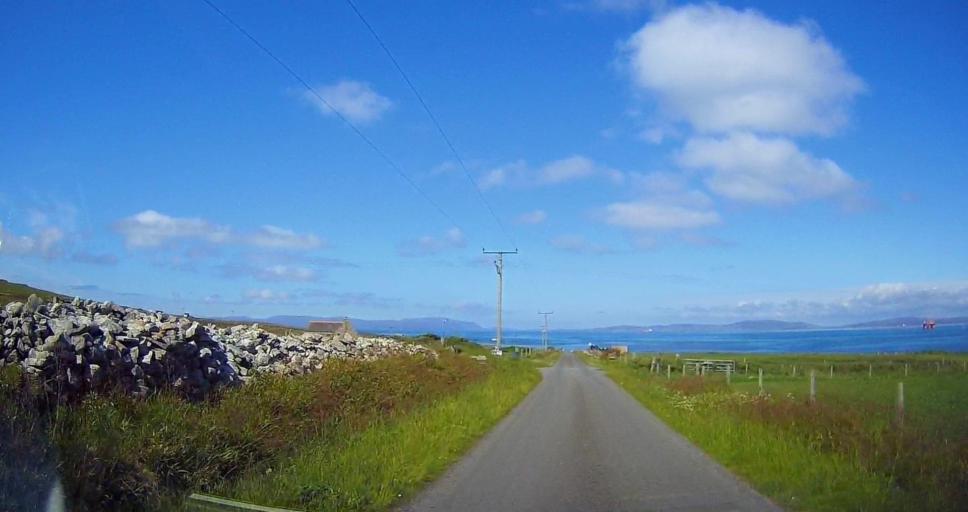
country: GB
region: Scotland
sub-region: Orkney Islands
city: Kirkwall
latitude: 58.8571
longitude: -2.9359
